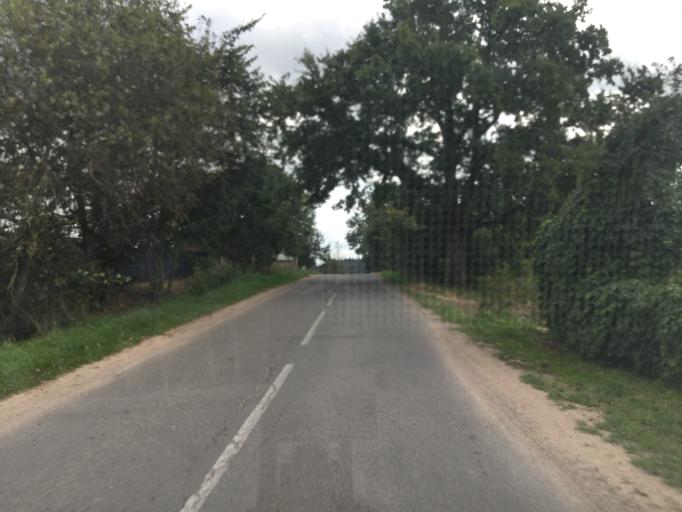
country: BY
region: Vitebsk
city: Vitebsk
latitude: 55.1443
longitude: 30.2853
